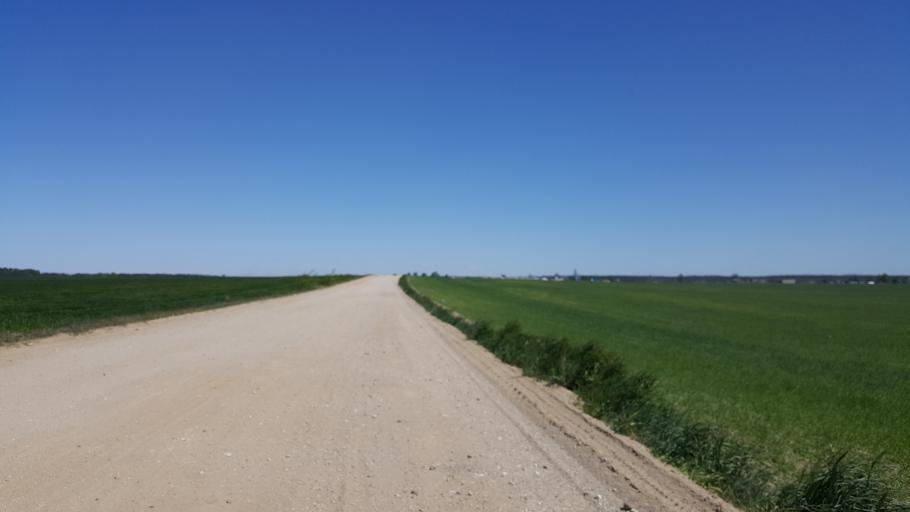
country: BY
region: Brest
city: Kamyanyuki
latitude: 52.4892
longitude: 23.7473
